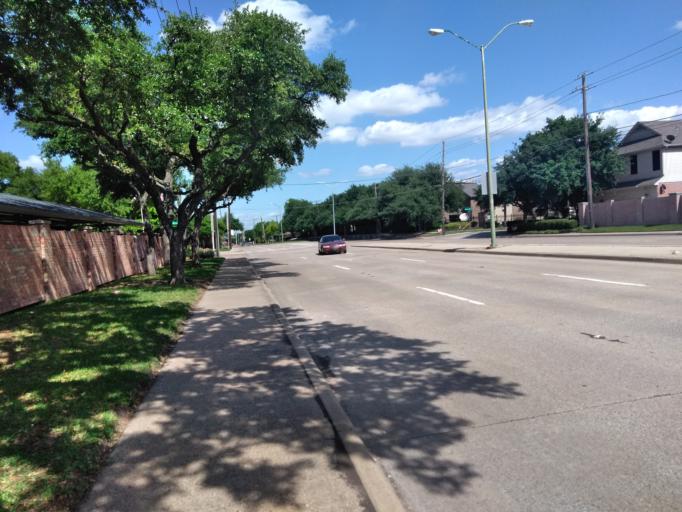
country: US
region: Texas
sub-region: Dallas County
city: Addison
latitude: 32.9982
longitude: -96.8021
